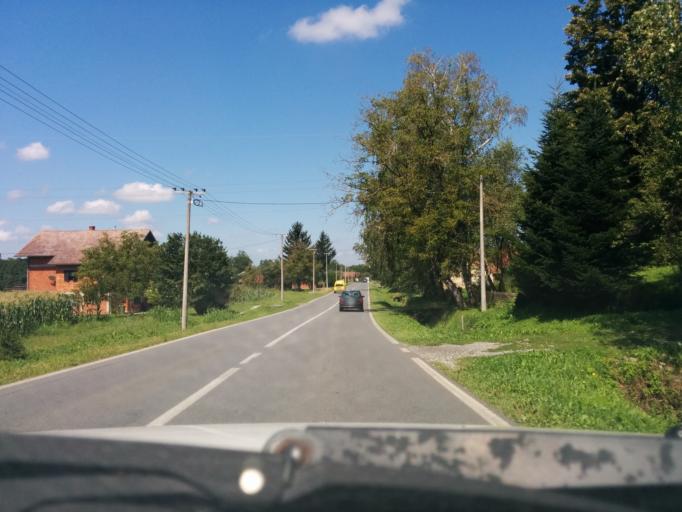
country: HR
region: Sisacko-Moslavacka
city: Lipovljani
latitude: 45.3791
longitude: 16.9114
